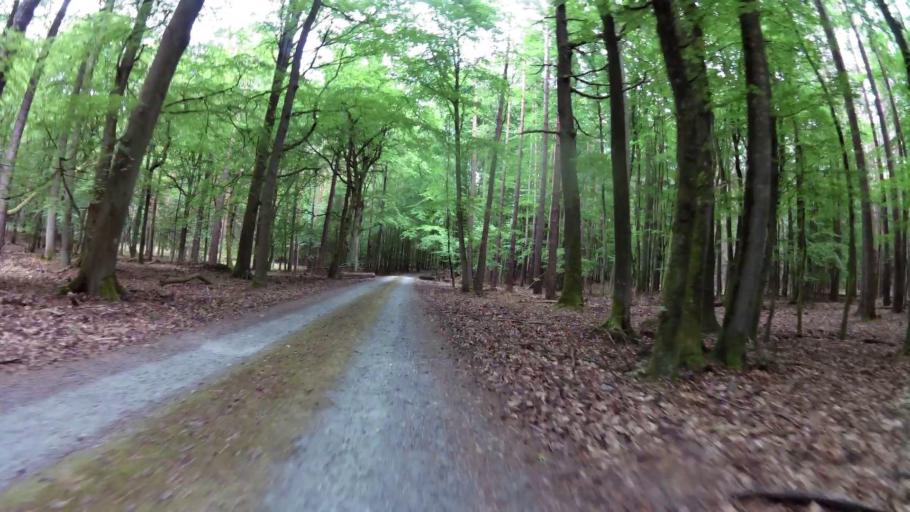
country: PL
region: West Pomeranian Voivodeship
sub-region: Powiat kamienski
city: Miedzyzdroje
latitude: 53.9425
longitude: 14.5043
